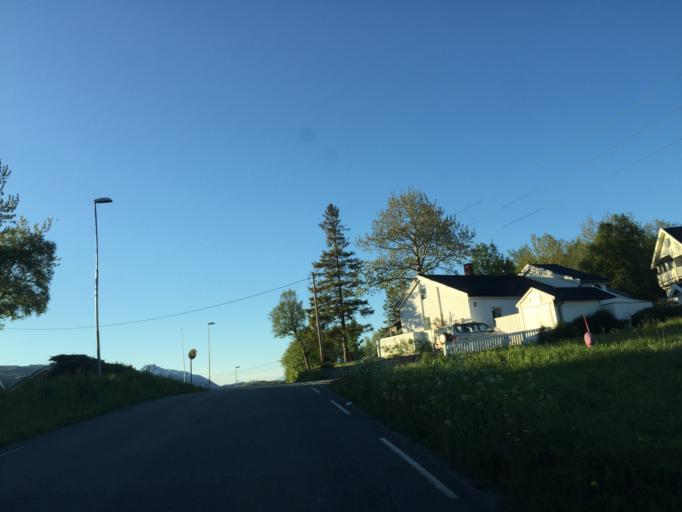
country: NO
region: Nordland
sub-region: Bodo
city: Loding
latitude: 67.2913
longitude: 14.7267
